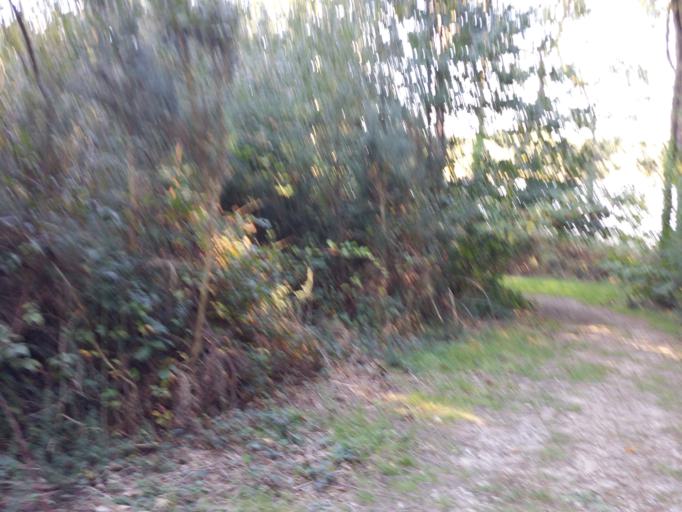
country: FR
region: Brittany
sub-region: Departement du Morbihan
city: Baden
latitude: 47.5965
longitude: -2.9235
